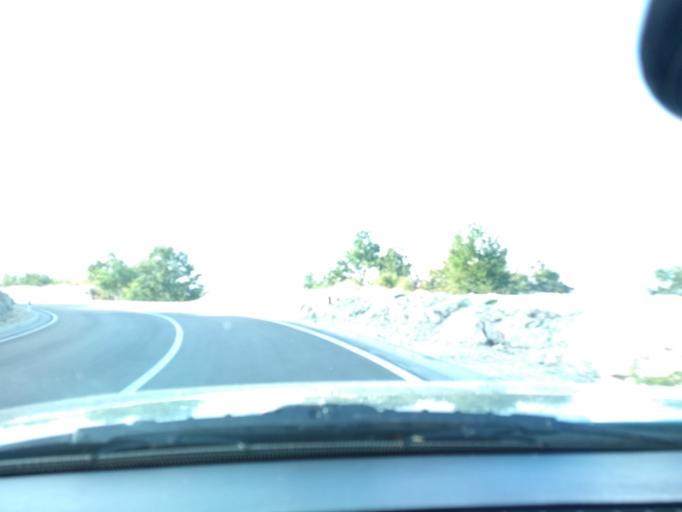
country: ME
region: Cetinje
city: Cetinje
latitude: 42.4114
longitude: 18.8878
